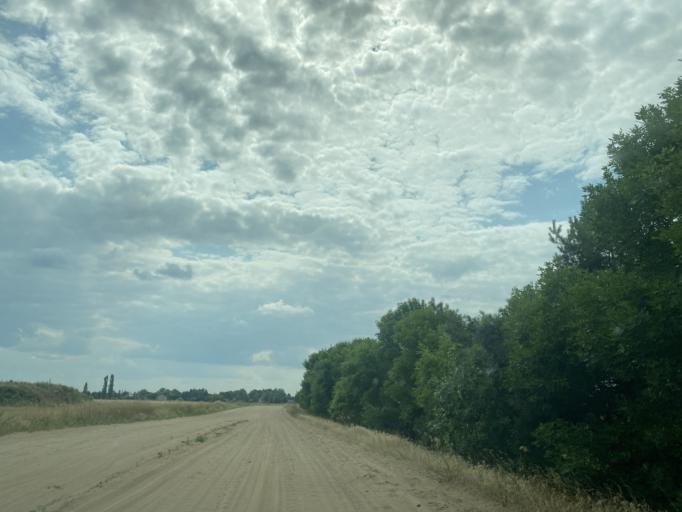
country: BY
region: Brest
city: Ivanava
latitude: 52.3583
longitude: 25.6327
